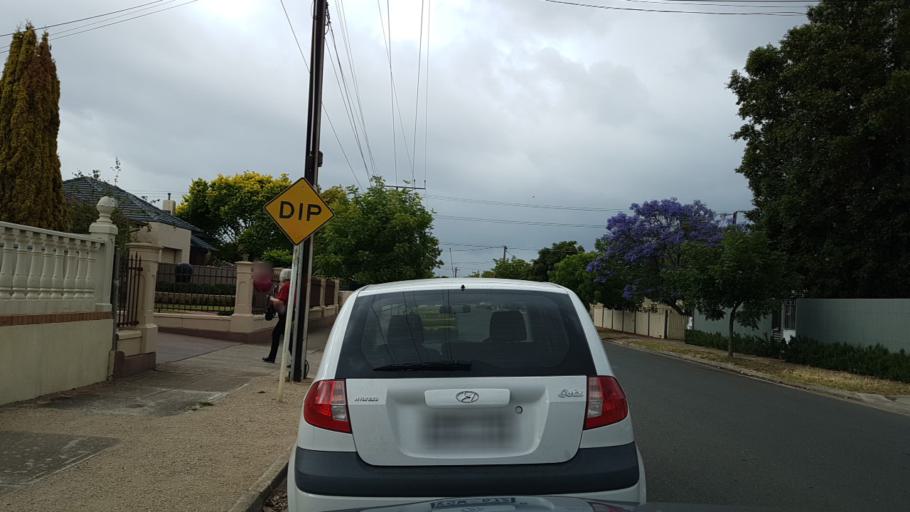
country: AU
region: South Australia
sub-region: City of West Torrens
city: Plympton
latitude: -34.9608
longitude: 138.5501
